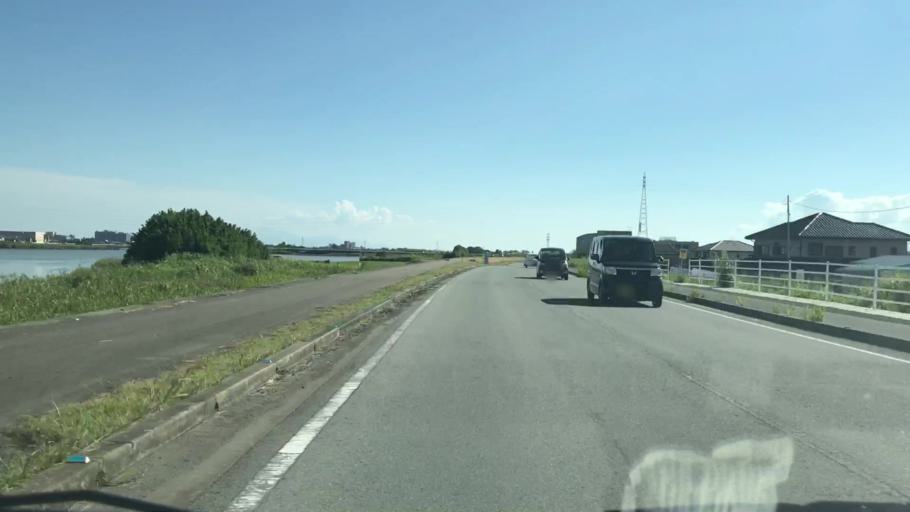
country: JP
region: Saga Prefecture
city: Okawa
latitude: 33.2348
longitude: 130.3795
